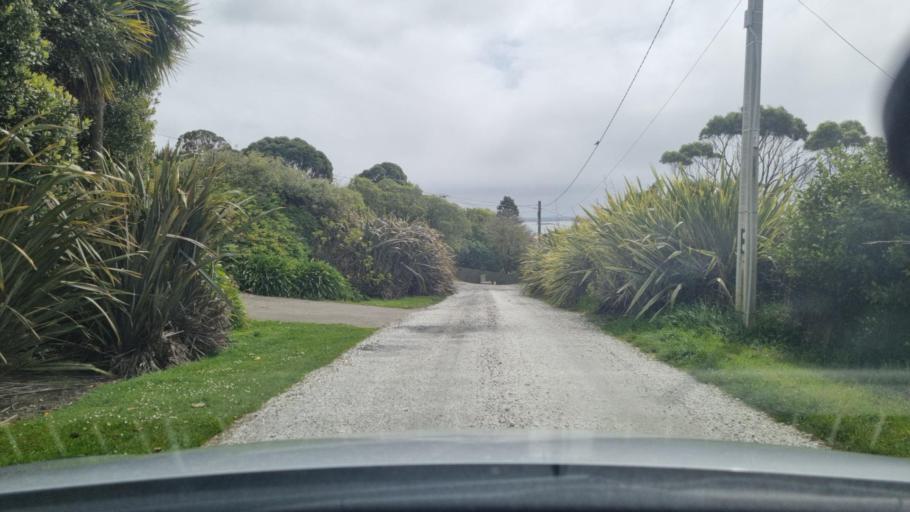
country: NZ
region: Southland
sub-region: Invercargill City
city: Bluff
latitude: -46.6075
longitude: 168.3509
